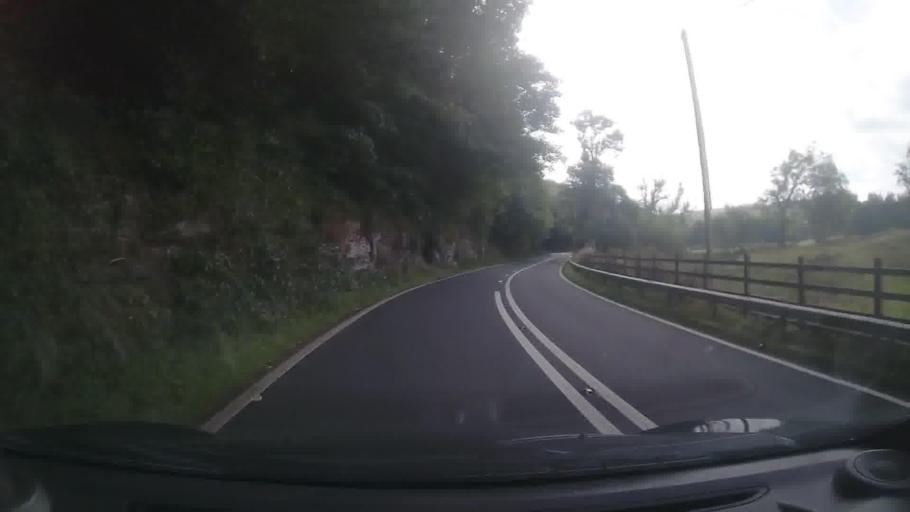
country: GB
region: Wales
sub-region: Sir Powys
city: Mochdre
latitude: 52.4070
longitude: -3.3445
